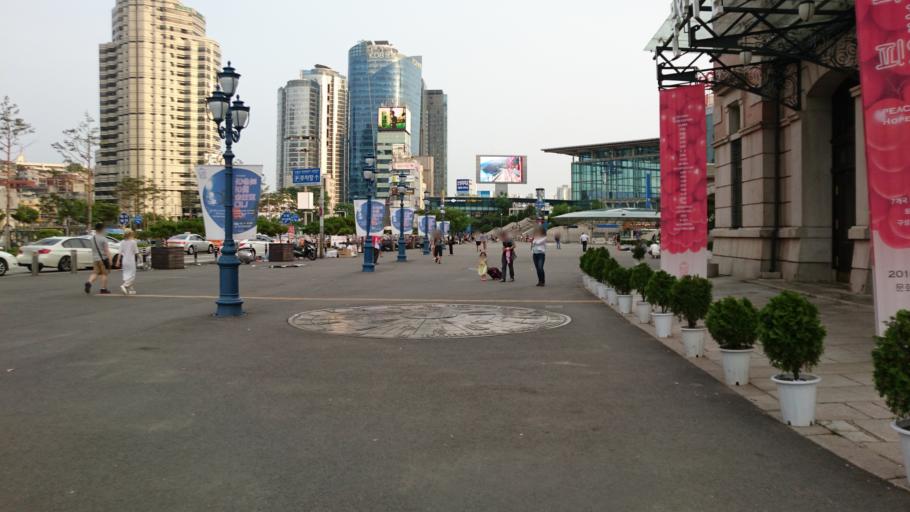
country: KR
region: Seoul
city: Seoul
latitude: 37.5560
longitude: 126.9719
